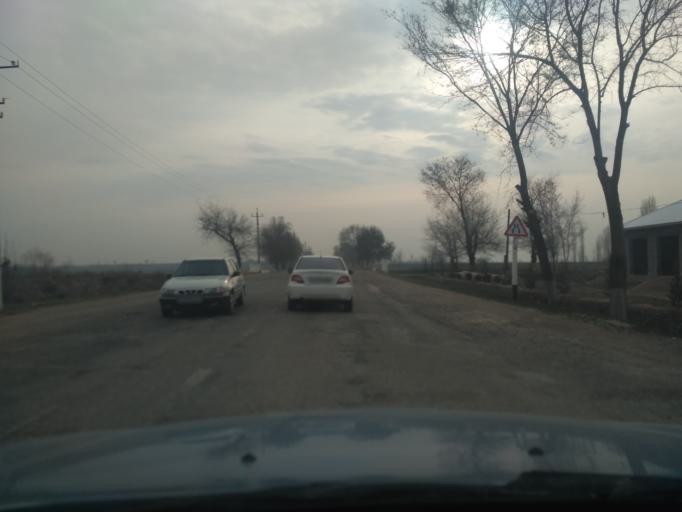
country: UZ
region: Sirdaryo
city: Sirdaryo
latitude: 40.8263
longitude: 68.6060
